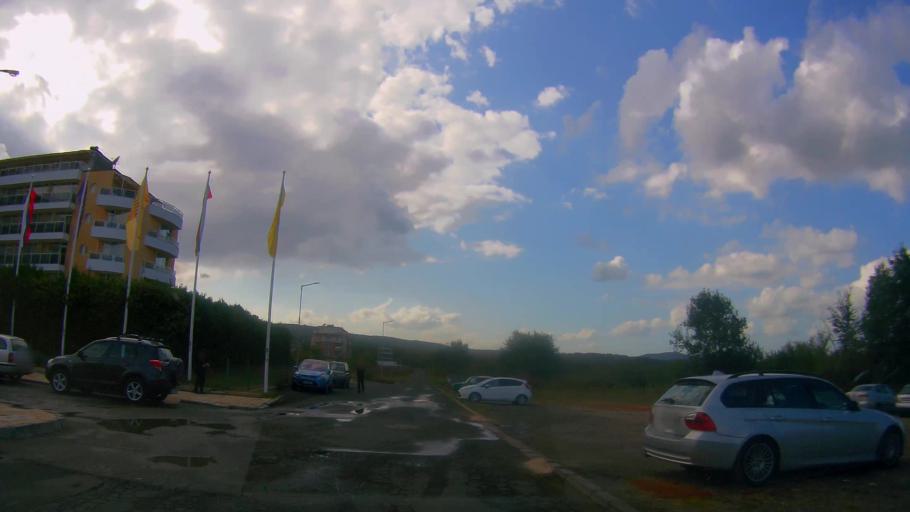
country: BG
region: Burgas
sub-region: Obshtina Primorsko
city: Primorsko
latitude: 42.2739
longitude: 27.7523
